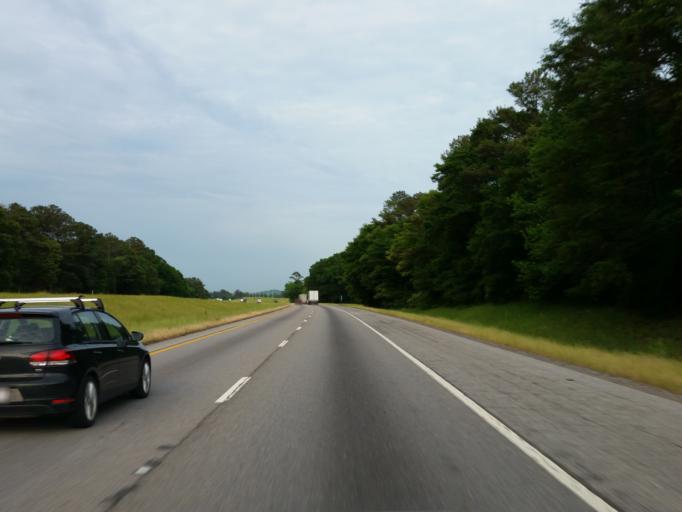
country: US
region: Alabama
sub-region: Talladega County
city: Lincoln
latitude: 33.5849
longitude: -86.0761
